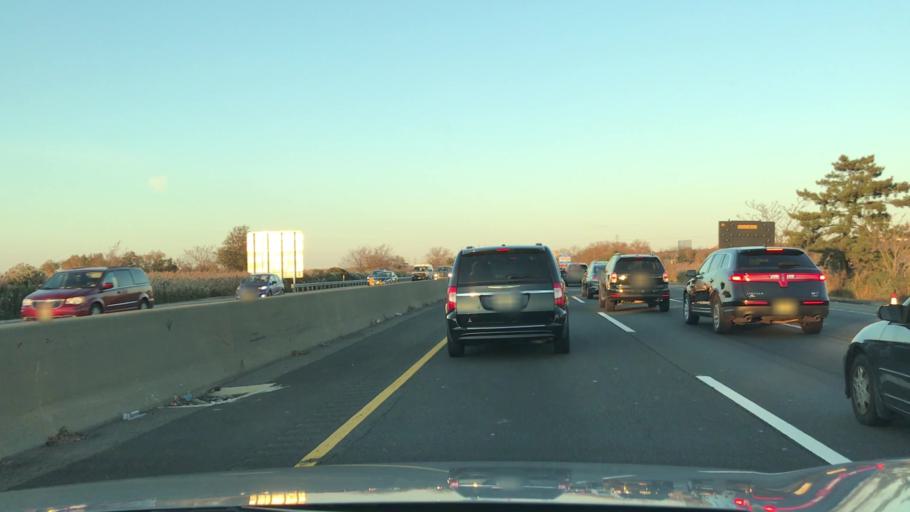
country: US
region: New Jersey
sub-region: Hudson County
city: Secaucus
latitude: 40.8001
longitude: -74.0375
